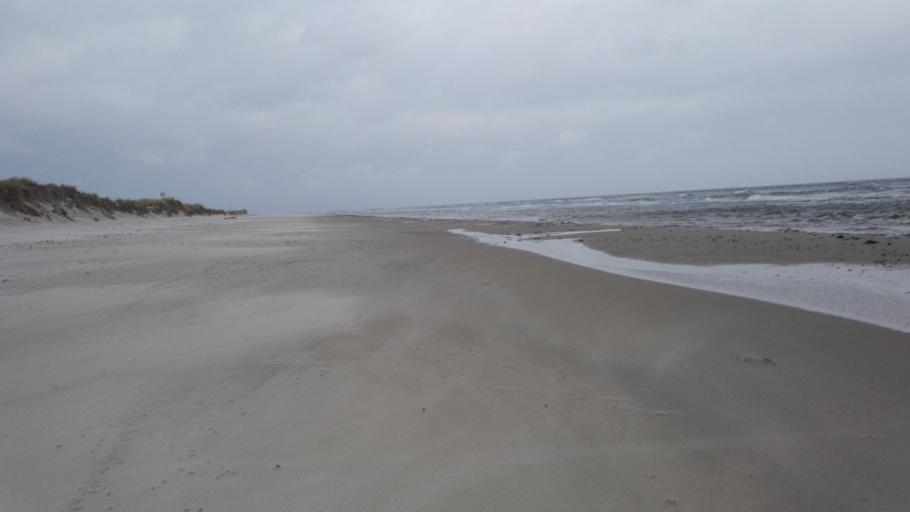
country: SE
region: Skane
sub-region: Simrishamns Kommun
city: Simrishamn
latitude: 55.3851
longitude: 14.1981
